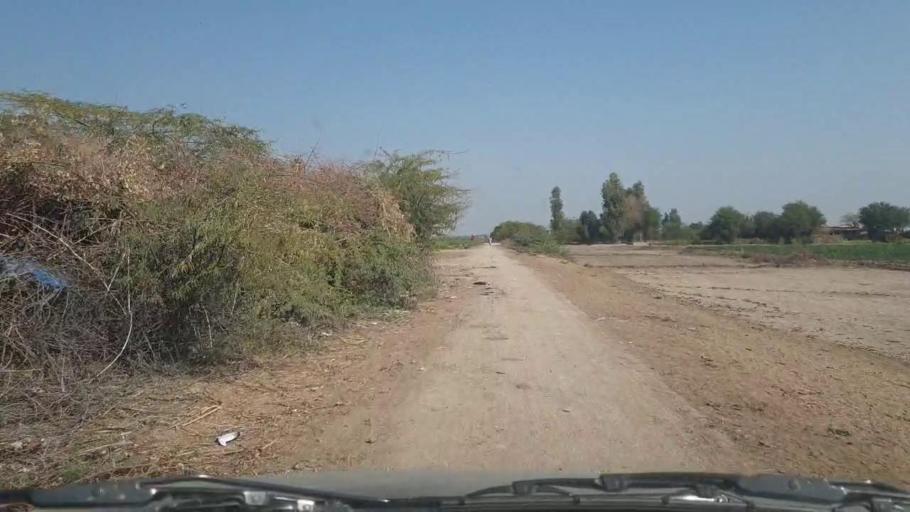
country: PK
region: Sindh
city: Samaro
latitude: 25.2802
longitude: 69.3142
